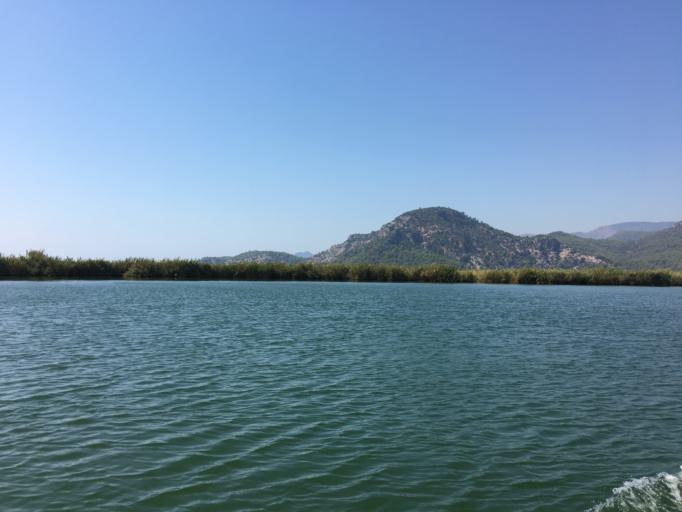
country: TR
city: Dalyan
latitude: 36.8155
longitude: 28.6294
